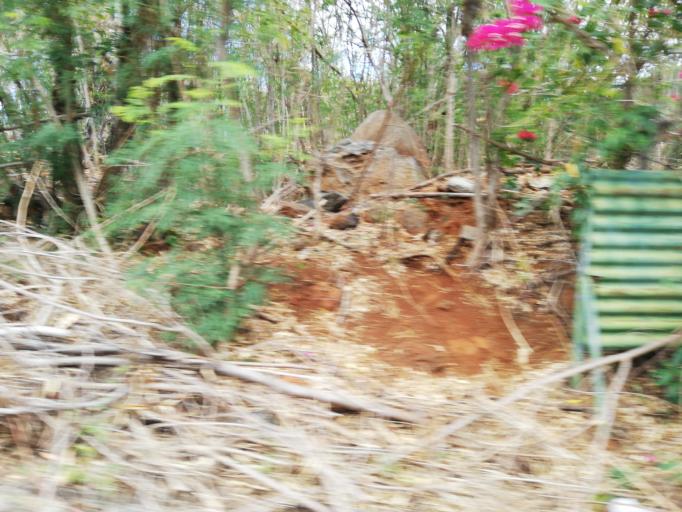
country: MU
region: Moka
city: Pailles
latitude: -20.1928
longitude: 57.4725
